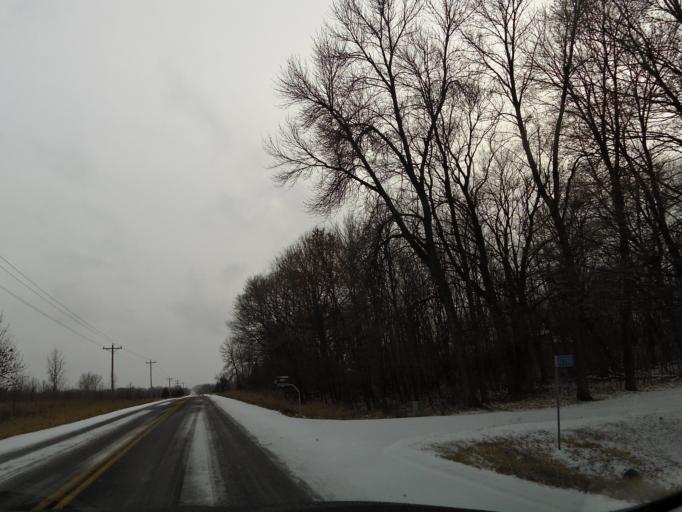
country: US
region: Minnesota
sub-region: Scott County
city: Prior Lake
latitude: 44.6923
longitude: -93.4603
